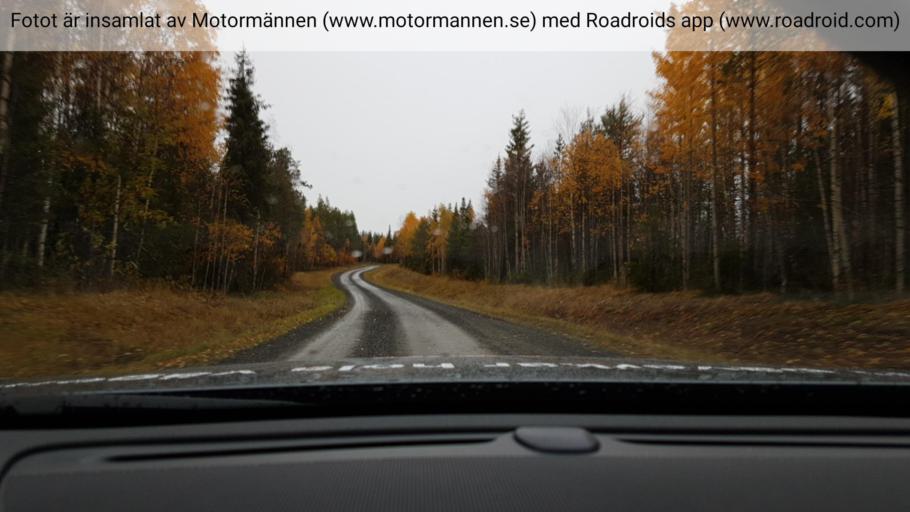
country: SE
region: Norrbotten
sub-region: Pajala Kommun
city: Pajala
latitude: 67.0603
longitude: 22.8312
